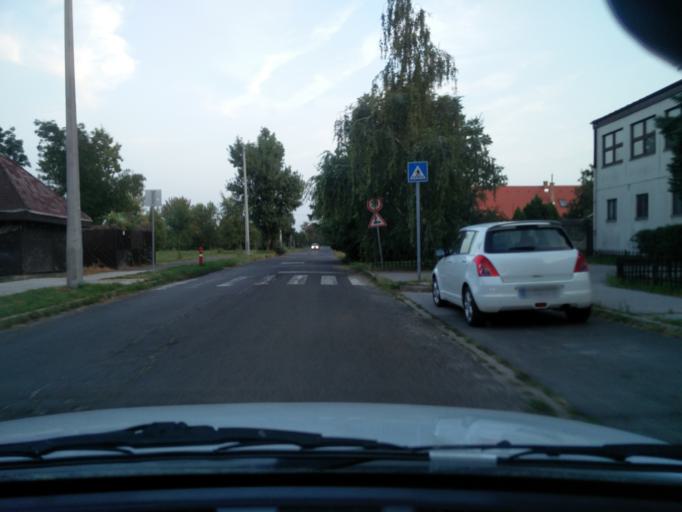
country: HU
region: Budapest
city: Budapest XX. keruelet
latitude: 47.4219
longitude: 19.0909
